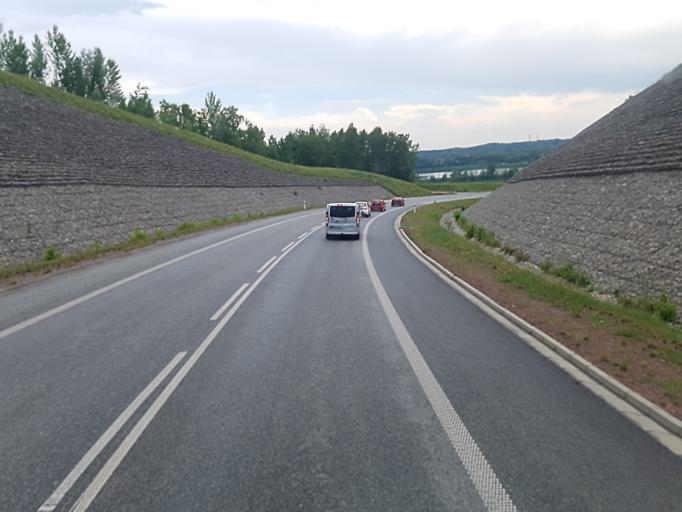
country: PL
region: Silesian Voivodeship
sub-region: Jastrzebie-Zdroj
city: Jastrzebie Zdroj
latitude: 49.9660
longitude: 18.5567
